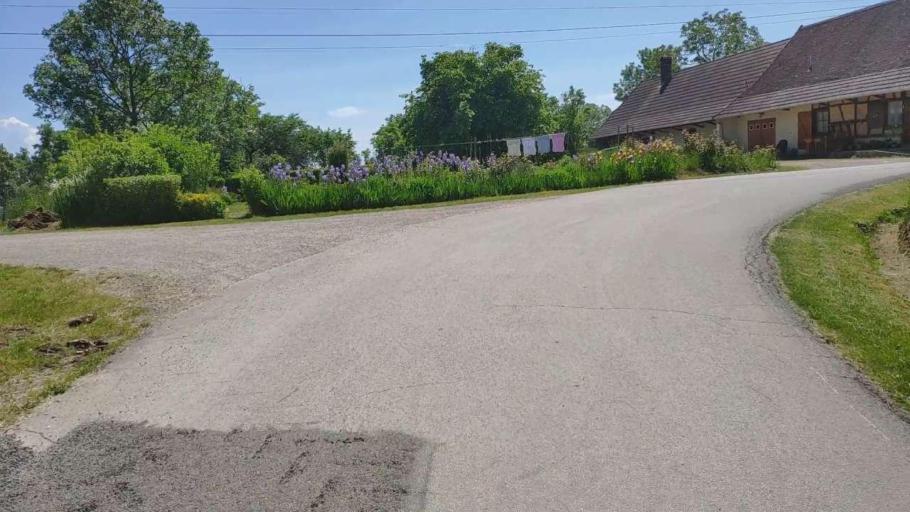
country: FR
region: Franche-Comte
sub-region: Departement du Jura
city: Bletterans
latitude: 46.7417
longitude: 5.3884
